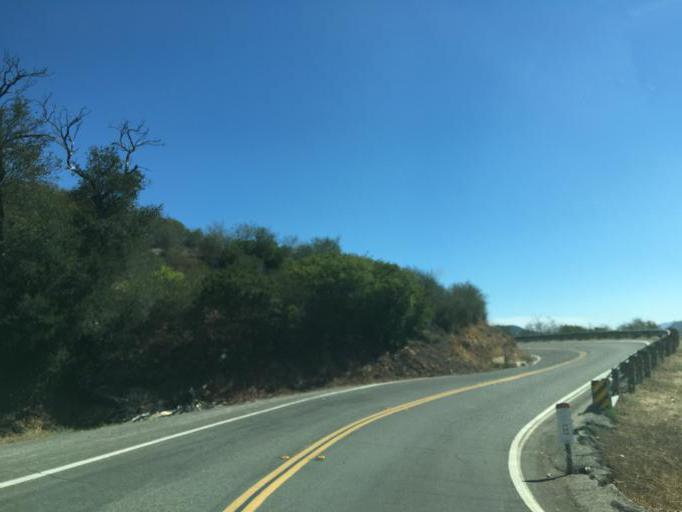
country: US
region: California
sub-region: Los Angeles County
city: Agoura Hills
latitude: 34.0667
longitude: -118.7549
